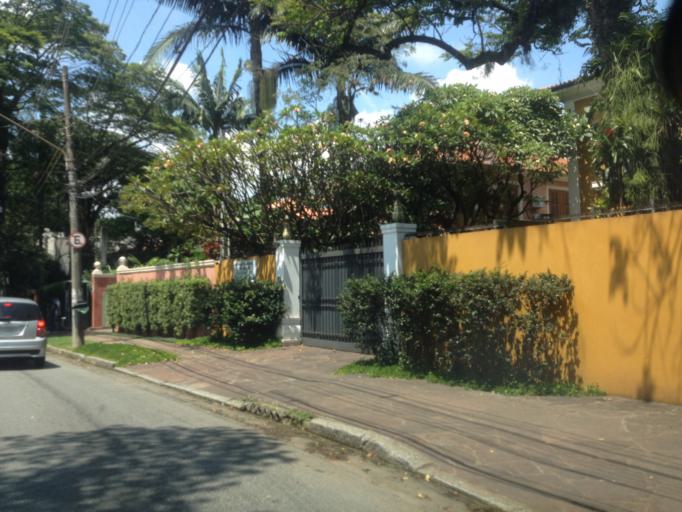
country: BR
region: Sao Paulo
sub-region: Sao Paulo
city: Sao Paulo
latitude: -23.5725
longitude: -46.6806
